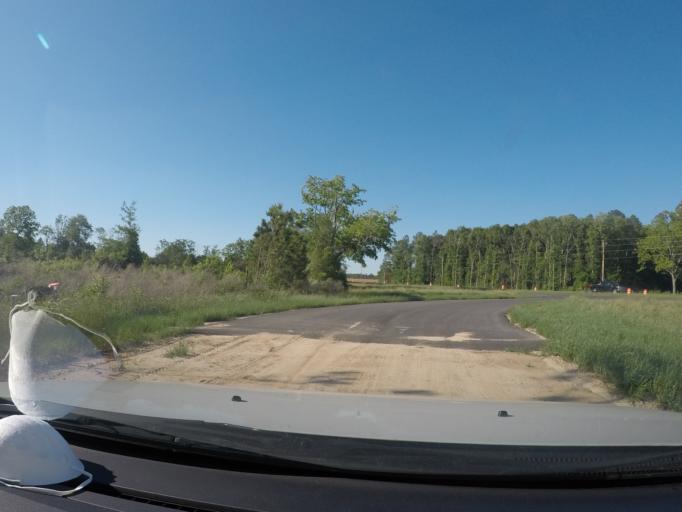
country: US
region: Georgia
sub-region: Bulloch County
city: Brooklet
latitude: 32.3455
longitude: -81.7405
